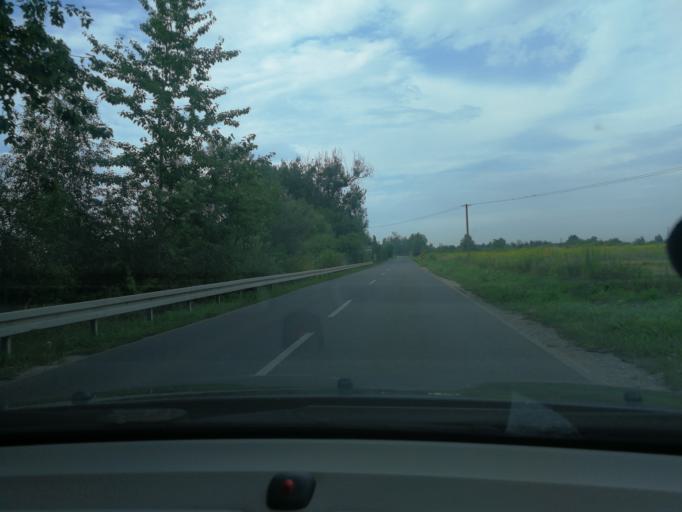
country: PL
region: Masovian Voivodeship
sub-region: Powiat grodziski
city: Grodzisk Mazowiecki
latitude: 52.1429
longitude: 20.6326
